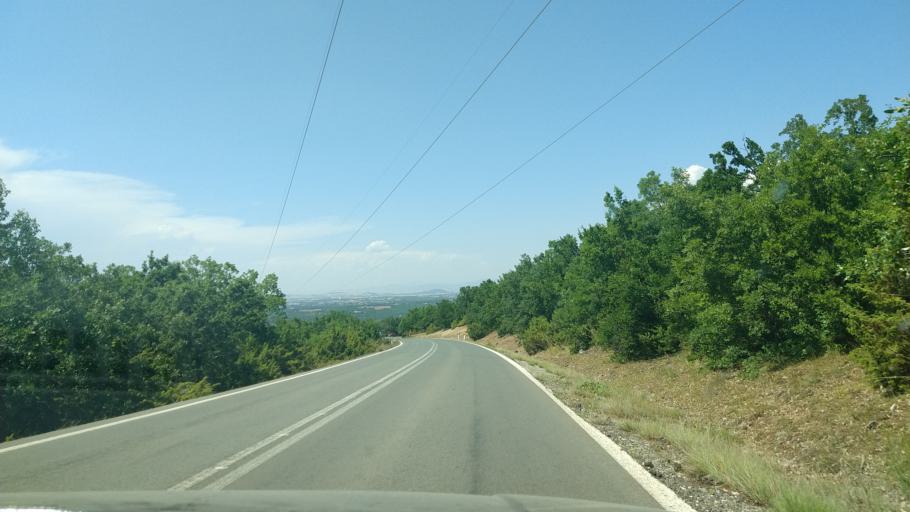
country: GR
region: West Macedonia
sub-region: Nomos Grevenon
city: Grevena
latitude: 40.0297
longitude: 21.4832
